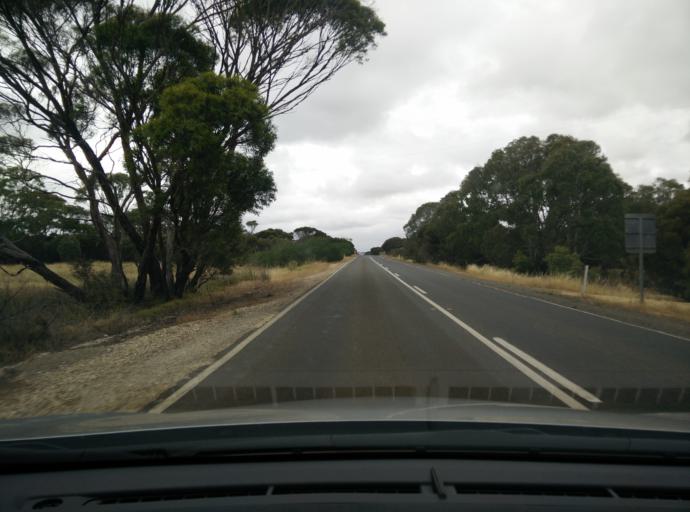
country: AU
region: South Australia
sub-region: Kangaroo Island
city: Kingscote
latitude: -35.6835
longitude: 137.5728
